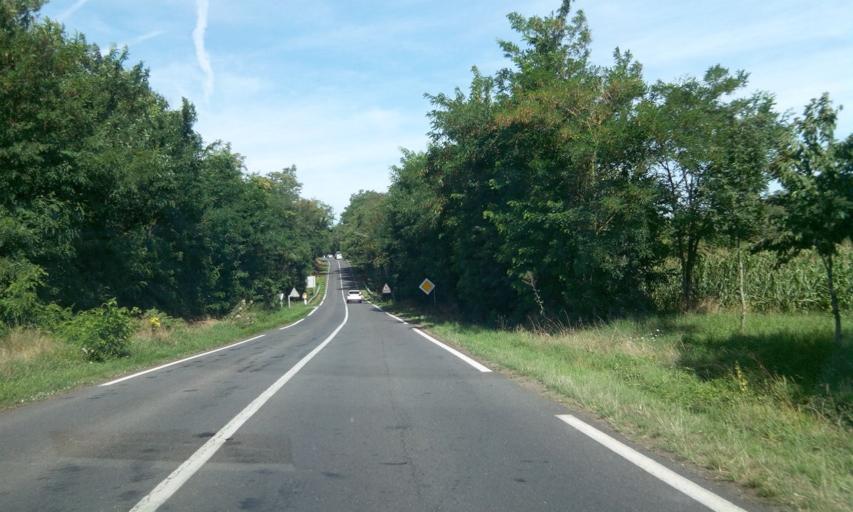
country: FR
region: Poitou-Charentes
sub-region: Departement de la Vienne
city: Charroux
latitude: 46.1533
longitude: 0.3720
